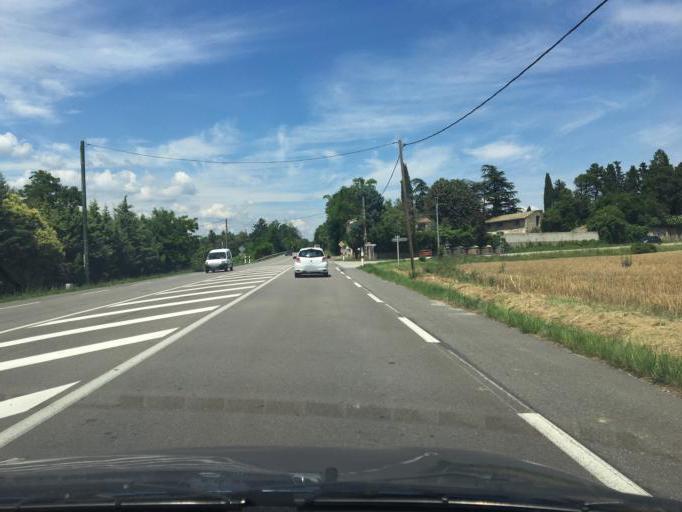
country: FR
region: Rhone-Alpes
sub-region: Departement de la Drome
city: Saulce-sur-Rhone
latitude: 44.6974
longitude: 4.7986
